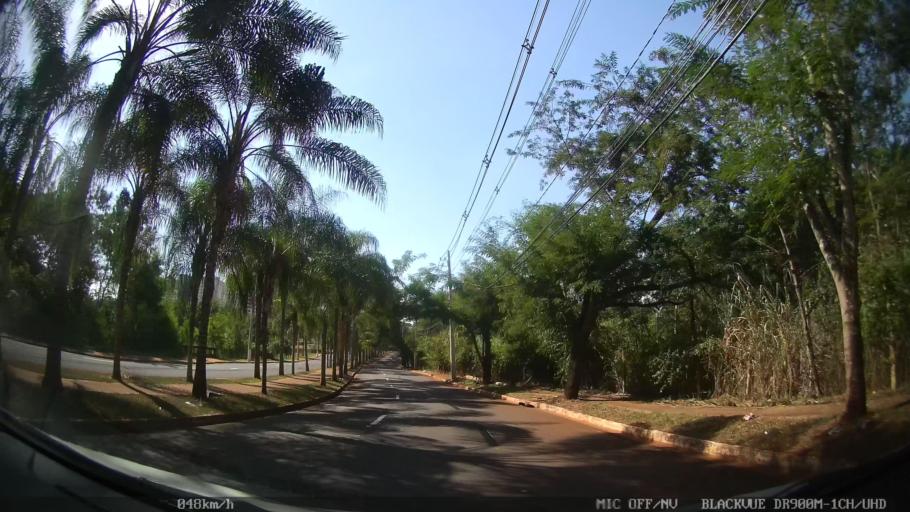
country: BR
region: Sao Paulo
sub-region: Ribeirao Preto
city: Ribeirao Preto
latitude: -21.2240
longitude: -47.8316
